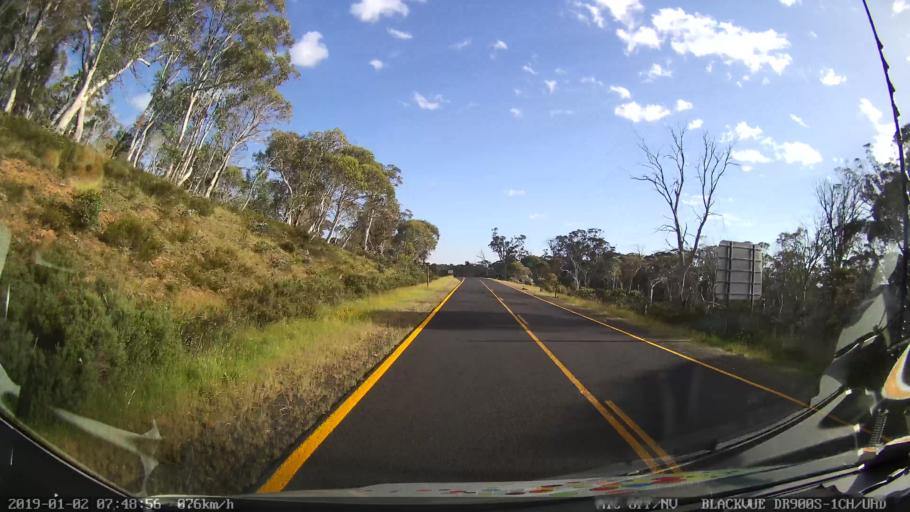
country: AU
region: New South Wales
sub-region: Tumut Shire
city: Tumut
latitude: -35.7475
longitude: 148.5206
